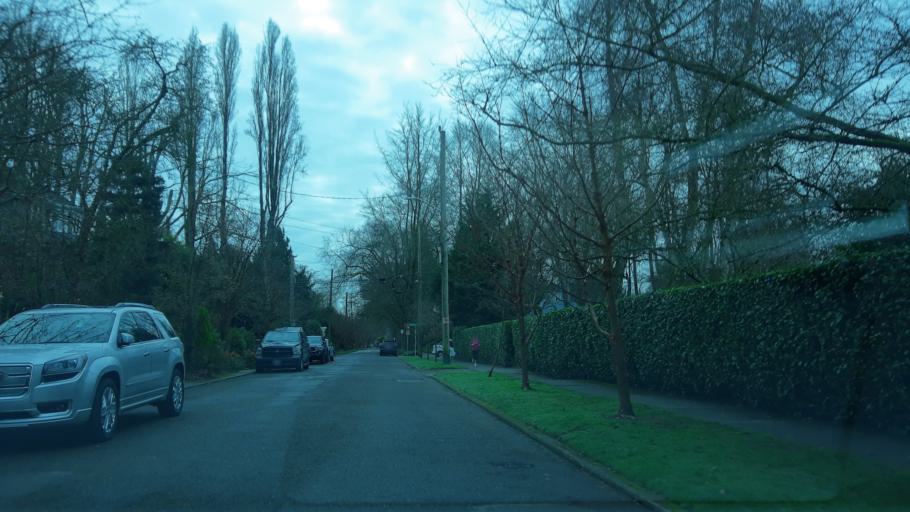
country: US
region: Washington
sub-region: King County
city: Seattle
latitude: 47.6294
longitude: -122.3224
